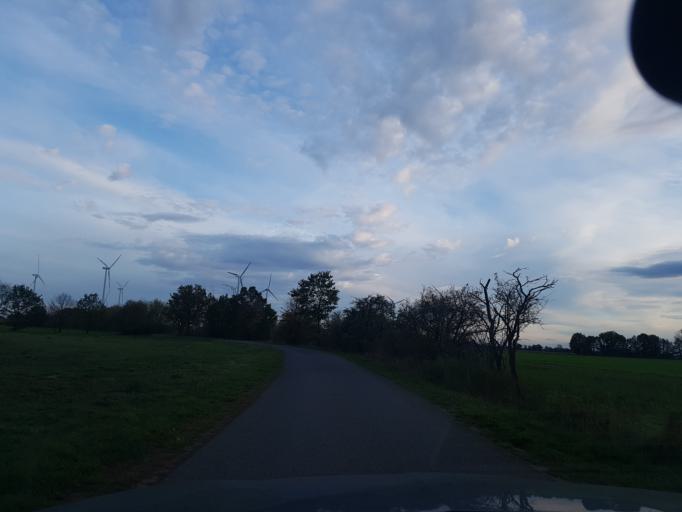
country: DE
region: Brandenburg
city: Elsterwerda
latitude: 51.4571
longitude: 13.4684
